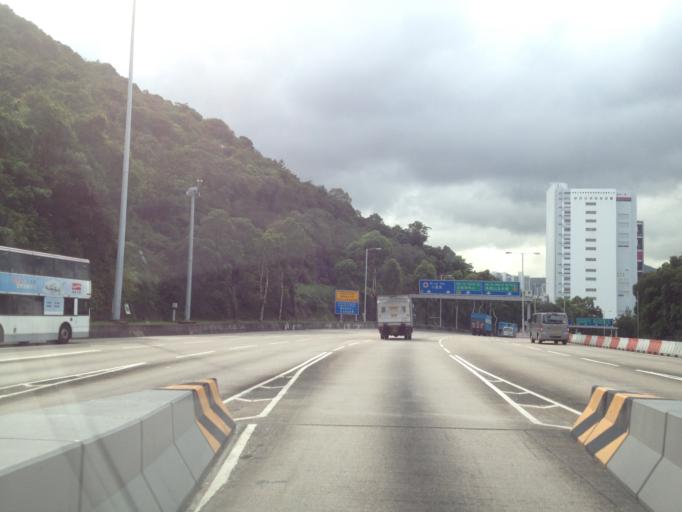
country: HK
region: Sha Tin
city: Sha Tin
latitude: 22.3774
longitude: 114.2116
